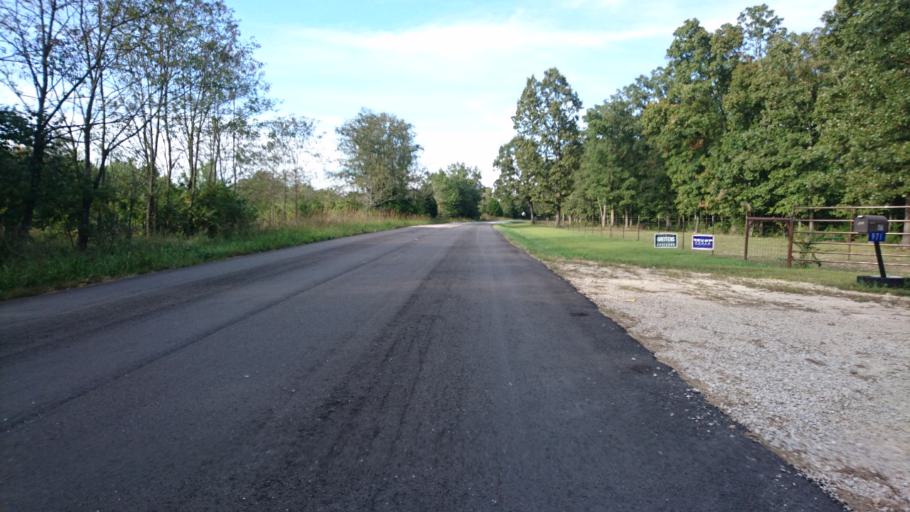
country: US
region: Missouri
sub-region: Crawford County
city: Cuba
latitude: 38.1044
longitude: -91.3628
